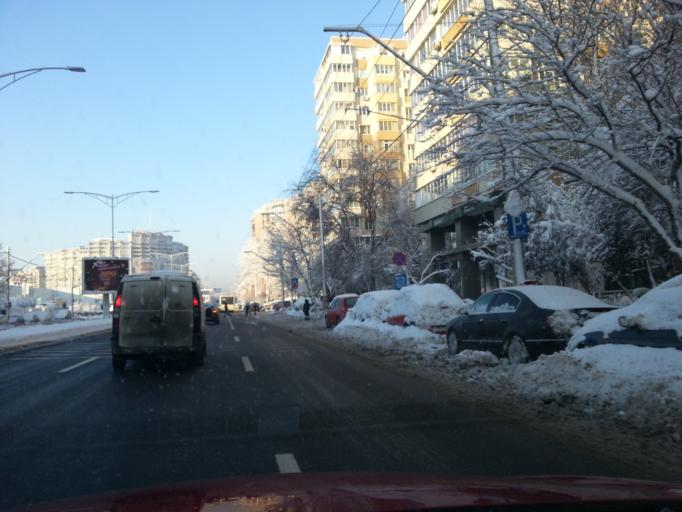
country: RO
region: Ilfov
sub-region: Comuna Chiajna
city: Rosu
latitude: 44.4343
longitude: 26.0396
